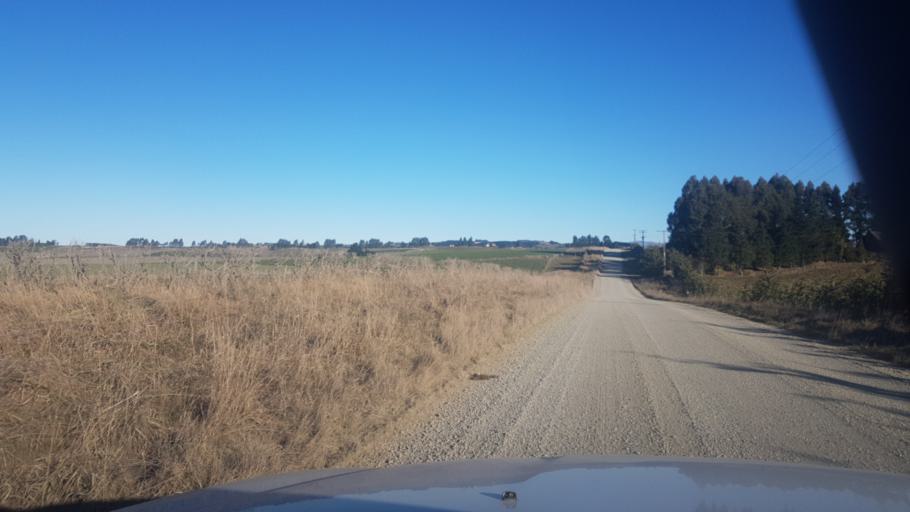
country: NZ
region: Canterbury
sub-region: Timaru District
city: Pleasant Point
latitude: -44.3486
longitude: 171.0737
